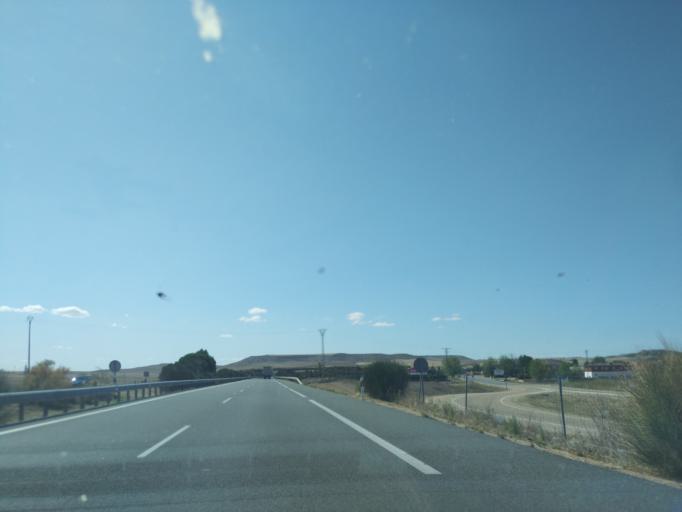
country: ES
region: Castille and Leon
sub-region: Provincia de Valladolid
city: Mota del Marques
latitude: 41.6259
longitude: -5.1756
